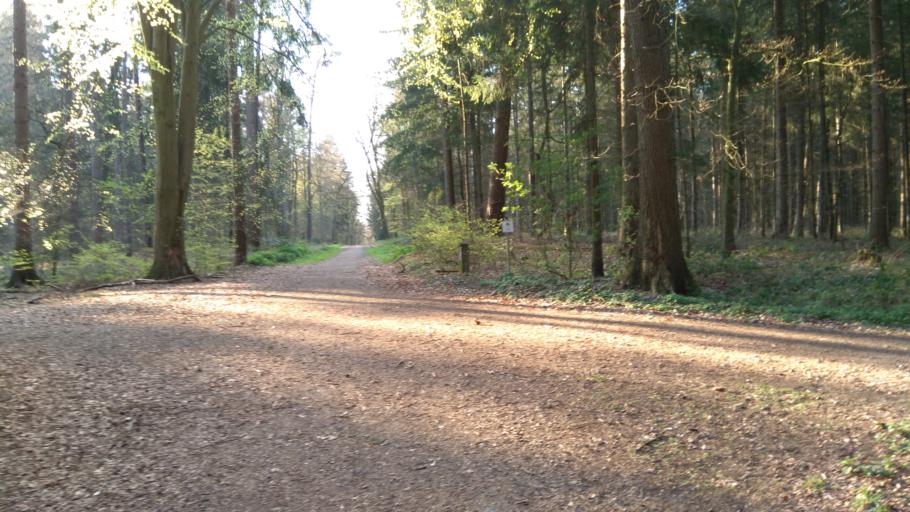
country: DE
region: Lower Saxony
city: Buxtehude
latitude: 53.4690
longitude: 9.6529
